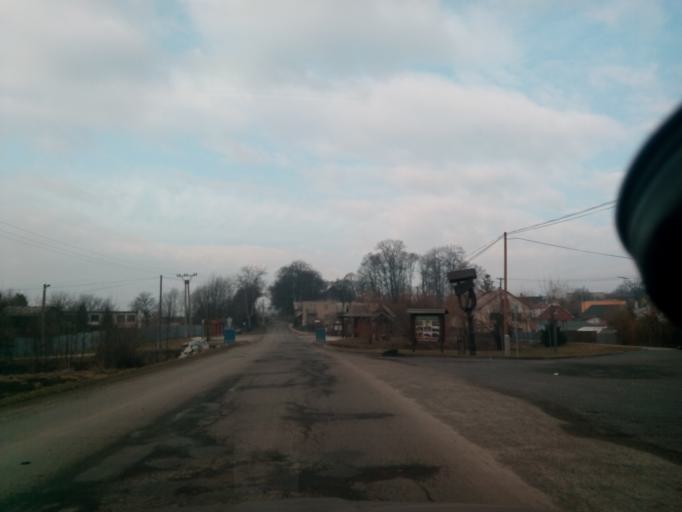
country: SK
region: Presovsky
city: Lipany
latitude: 49.1691
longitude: 20.9187
